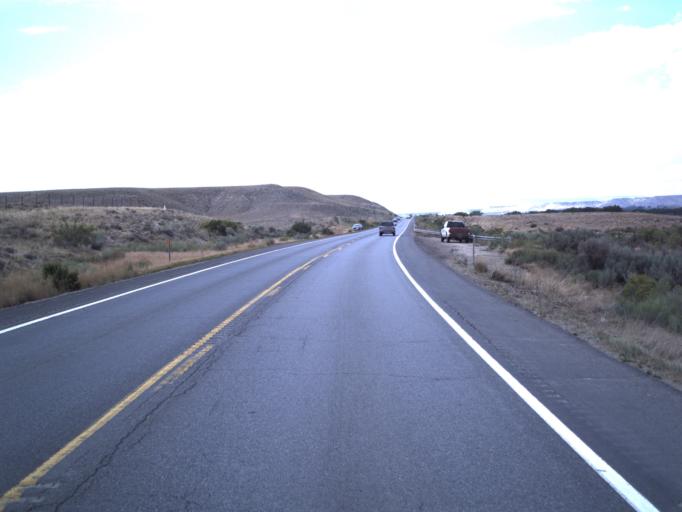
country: US
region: Utah
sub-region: Duchesne County
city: Duchesne
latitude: 40.1532
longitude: -110.2408
